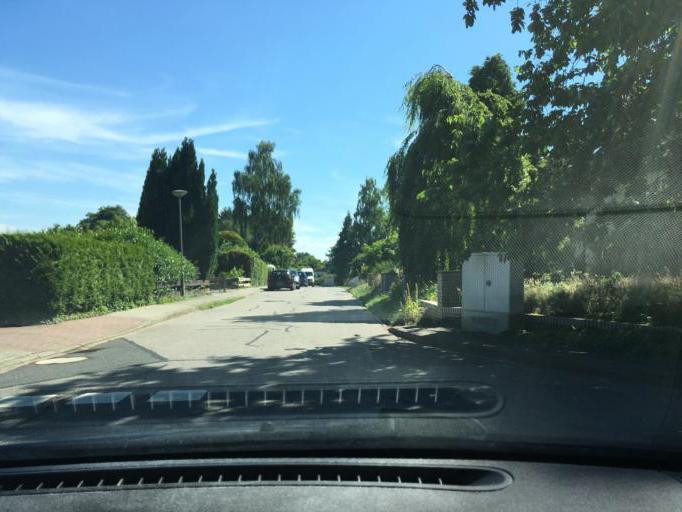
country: DE
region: Lower Saxony
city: Buchholz in der Nordheide
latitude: 53.3810
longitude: 9.8860
